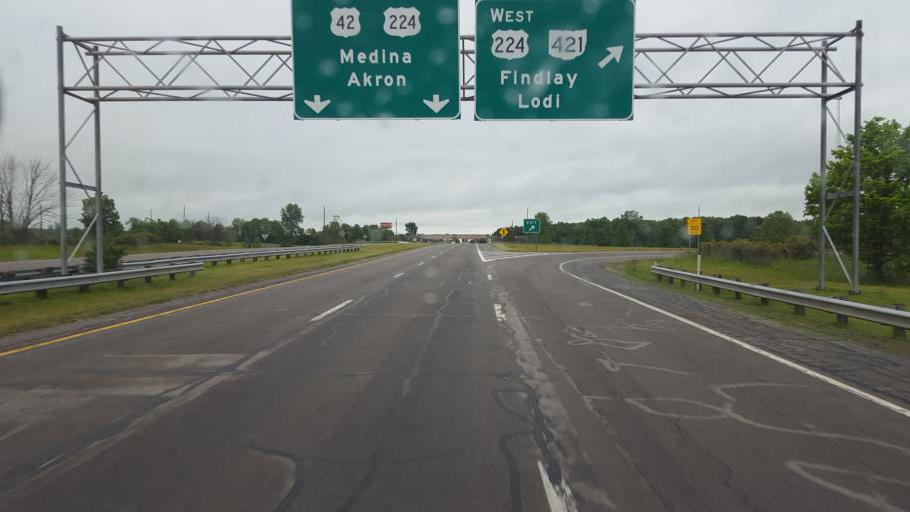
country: US
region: Ohio
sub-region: Medina County
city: Lodi
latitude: 41.0242
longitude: -82.0519
